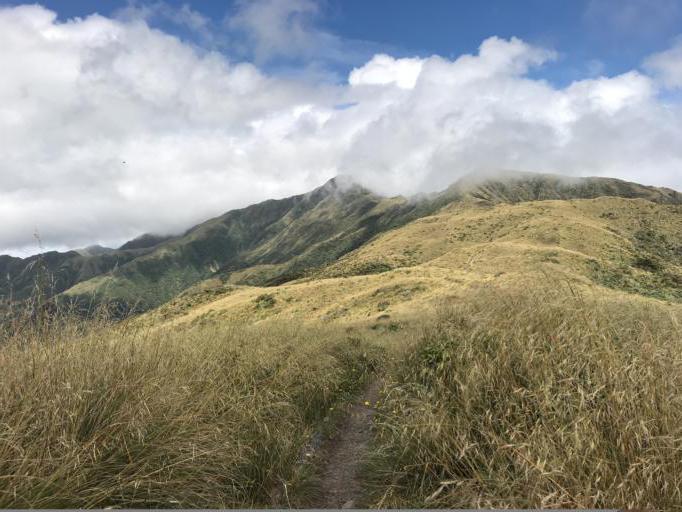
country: NZ
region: Wellington
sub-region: Kapiti Coast District
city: Otaki
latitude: -40.9125
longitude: 175.2629
